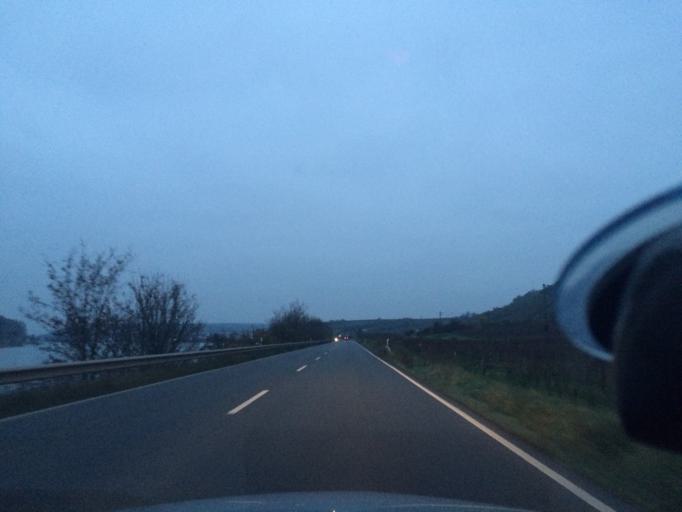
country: DE
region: Rheinland-Pfalz
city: Nierstein
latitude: 49.8909
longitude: 8.3394
